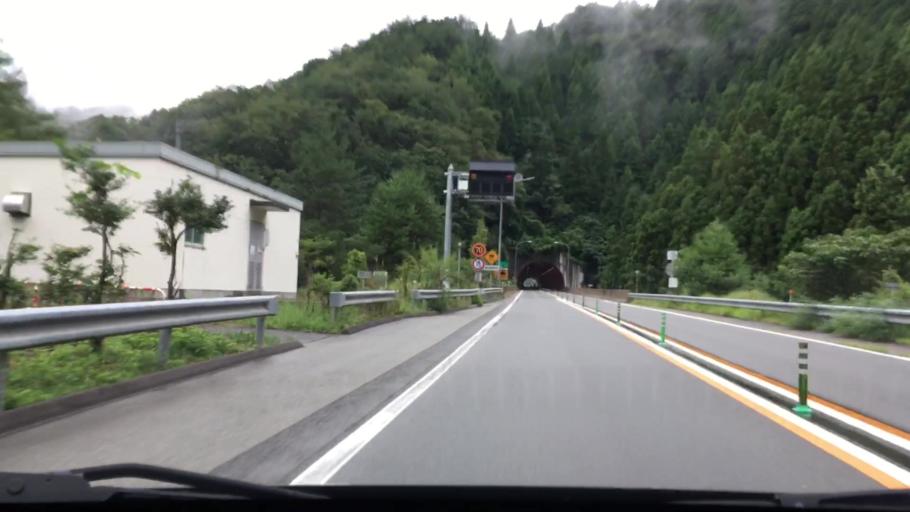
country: JP
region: Hyogo
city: Toyooka
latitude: 35.2566
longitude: 134.7943
